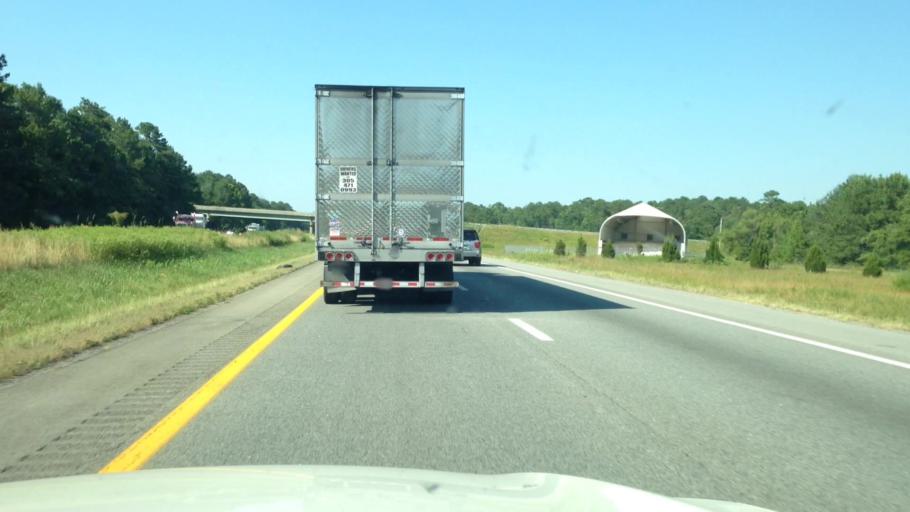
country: US
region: Virginia
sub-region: City of Emporia
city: Emporia
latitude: 36.7312
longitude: -77.5230
